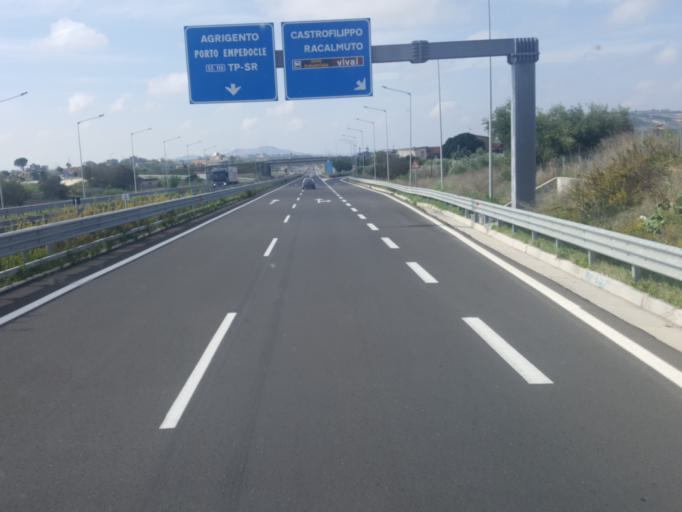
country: IT
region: Sicily
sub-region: Agrigento
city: Racalmuto
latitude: 37.3871
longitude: 13.7411
